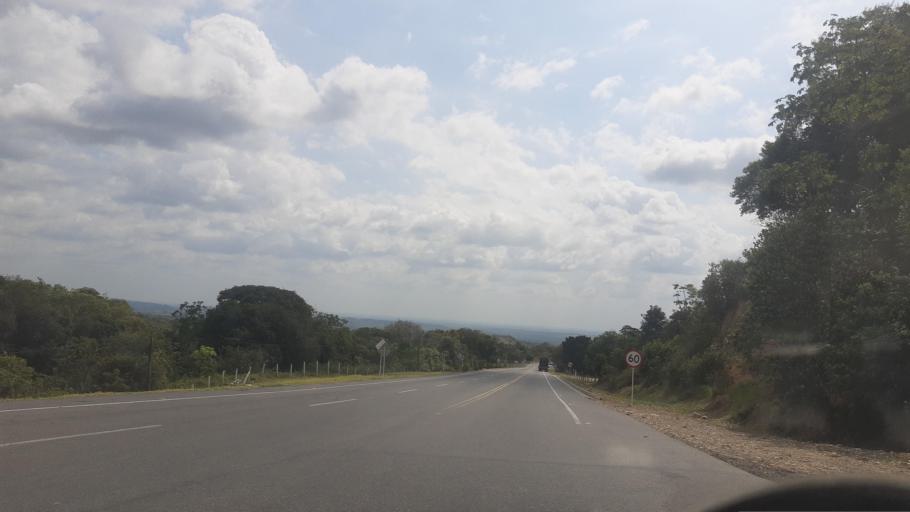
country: CO
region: Casanare
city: Monterrey
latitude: 4.8442
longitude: -72.8418
